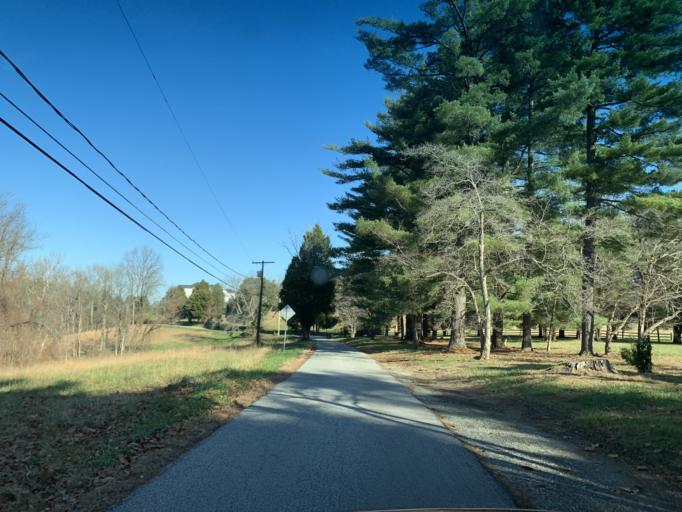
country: US
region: Maryland
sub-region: Harford County
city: Bel Air South
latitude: 39.4974
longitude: -76.3512
